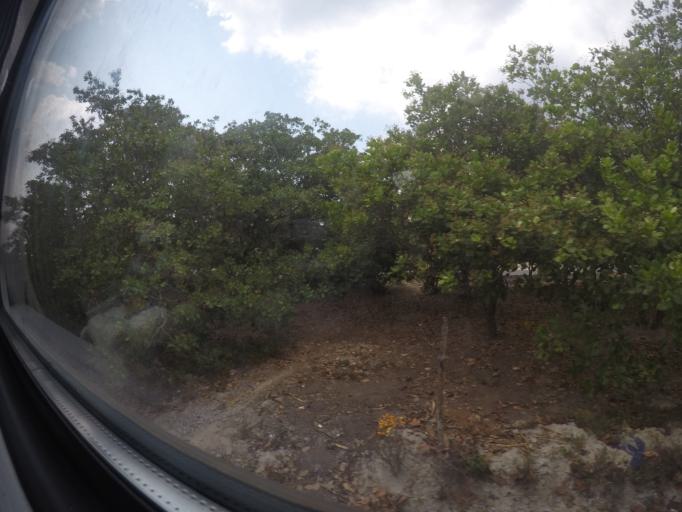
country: VN
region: Binh Thuan
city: Tanh Linh
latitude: 10.9635
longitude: 107.6389
